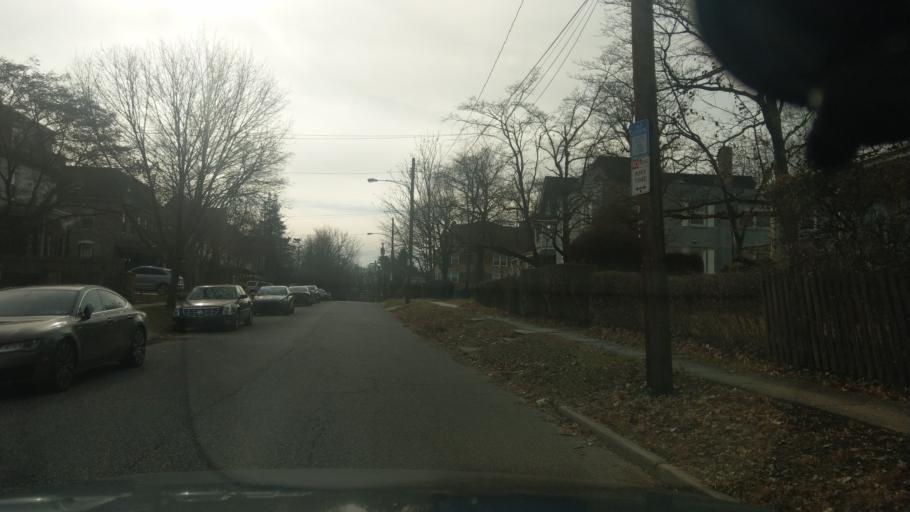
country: US
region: Pennsylvania
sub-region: Montgomery County
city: Jenkintown
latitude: 40.0540
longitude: -75.1316
